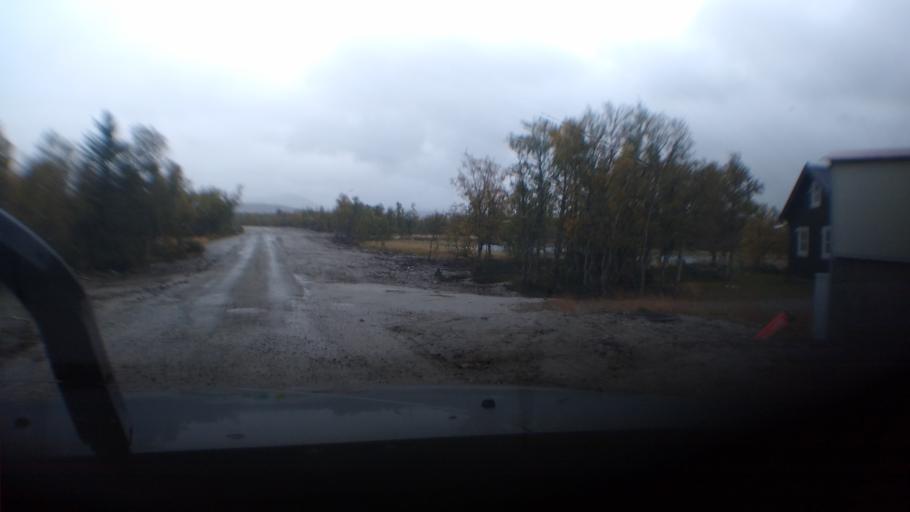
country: NO
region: Oppland
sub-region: Ringebu
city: Ringebu
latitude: 61.6537
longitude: 10.1018
